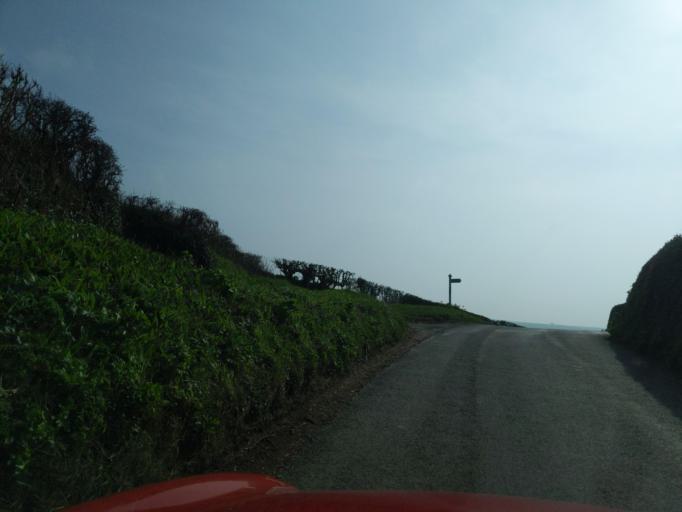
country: GB
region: England
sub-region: Devon
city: Salcombe
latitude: 50.2559
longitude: -3.7141
